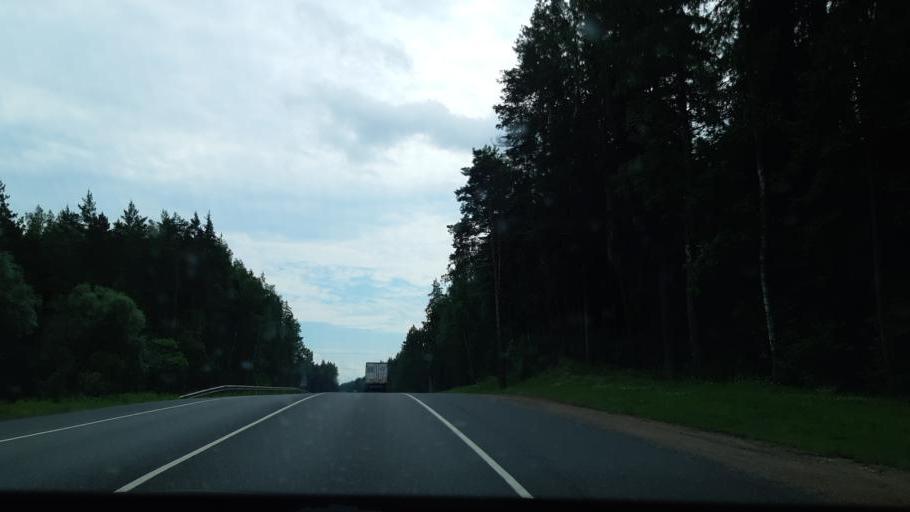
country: RU
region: Moskovskaya
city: Dorokhovo
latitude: 55.4526
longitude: 36.3525
